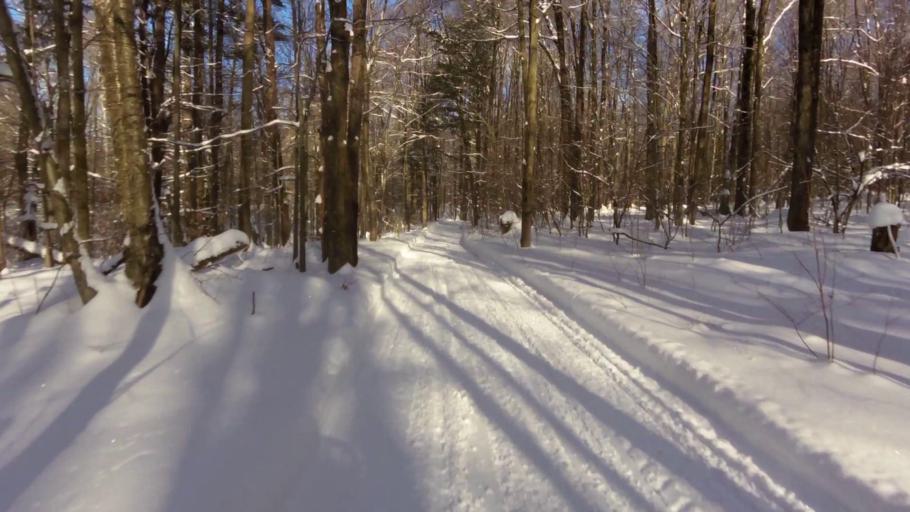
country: US
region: New York
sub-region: Chautauqua County
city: Falconer
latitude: 42.2587
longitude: -79.1440
